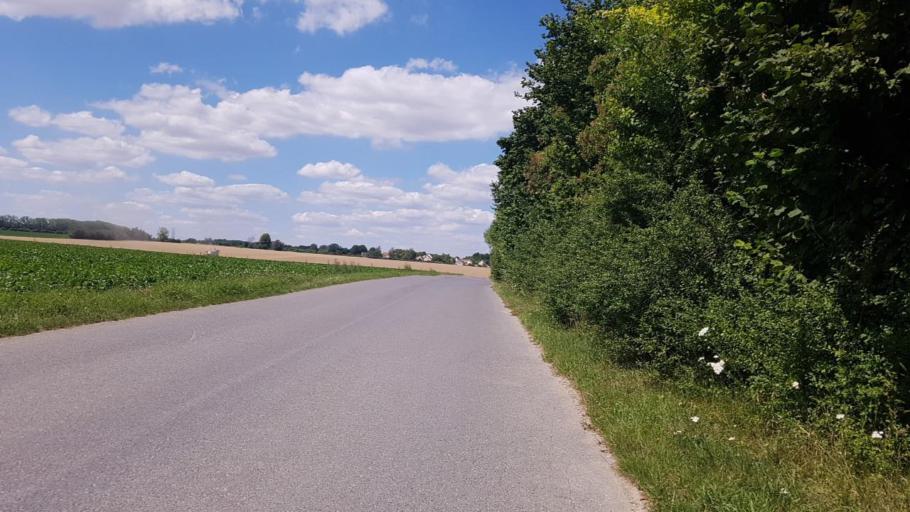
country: FR
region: Ile-de-France
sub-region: Departement de Seine-et-Marne
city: Claye-Souilly
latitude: 48.9833
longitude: 2.6696
